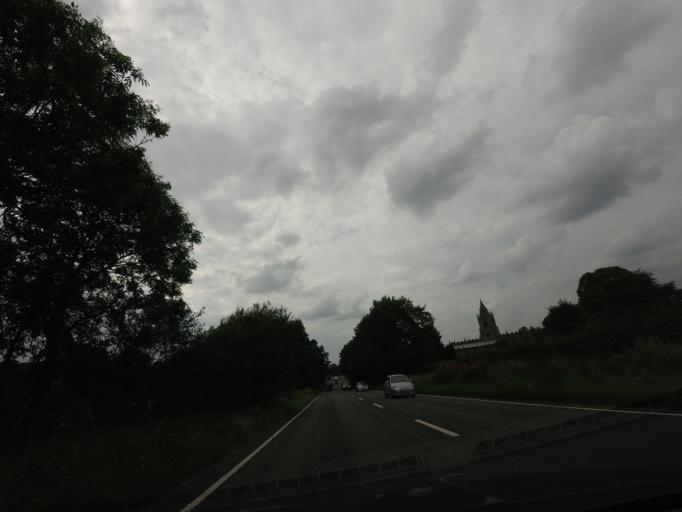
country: GB
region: England
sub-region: Shropshire
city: Tong
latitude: 52.6626
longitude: -2.3033
